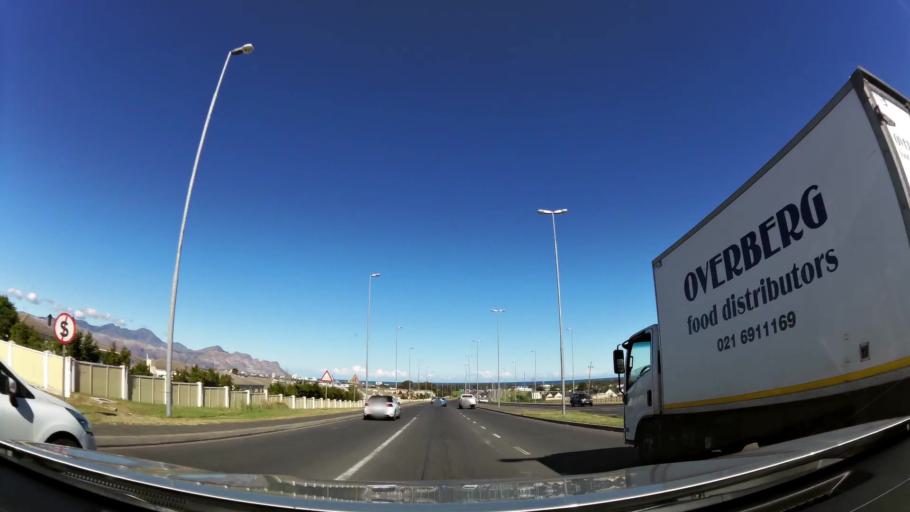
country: ZA
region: Western Cape
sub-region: Cape Winelands District Municipality
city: Stellenbosch
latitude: -34.0700
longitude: 18.8252
